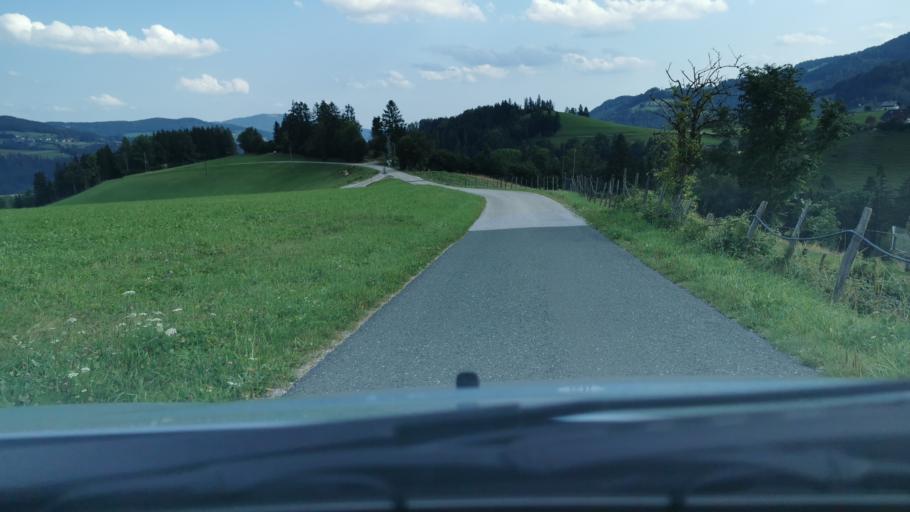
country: AT
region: Styria
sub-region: Politischer Bezirk Weiz
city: Koglhof
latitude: 47.3156
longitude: 15.6726
